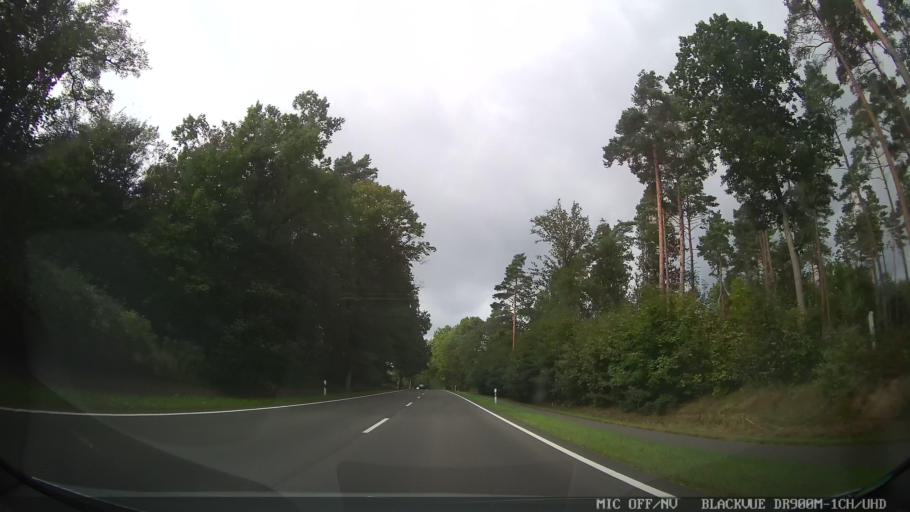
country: DE
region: Lower Saxony
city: Hambuhren
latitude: 52.6689
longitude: 10.0350
